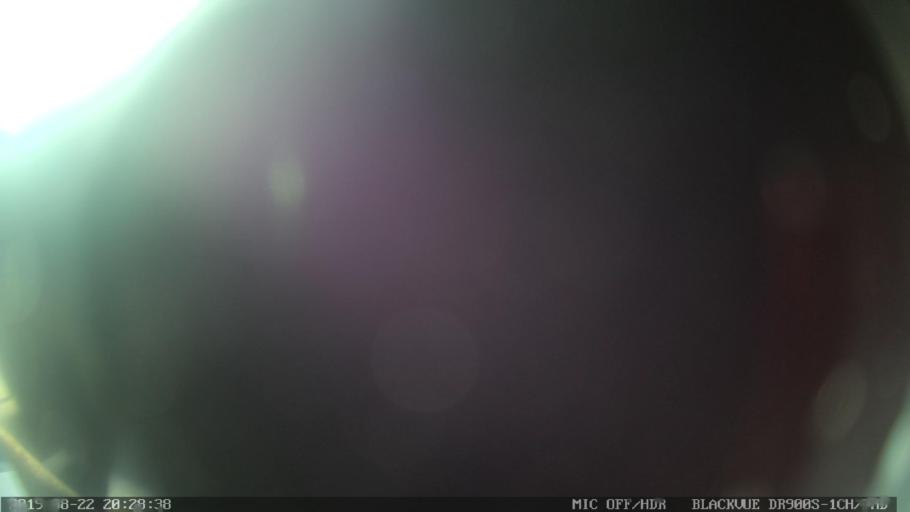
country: PT
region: Castelo Branco
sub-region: Castelo Branco
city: Castelo Branco
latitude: 39.7755
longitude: -7.5865
